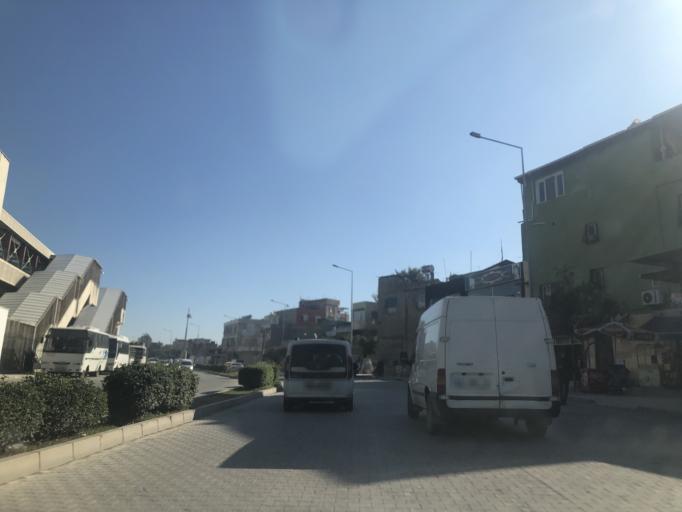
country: TR
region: Adana
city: Seyhan
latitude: 36.9788
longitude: 35.3249
